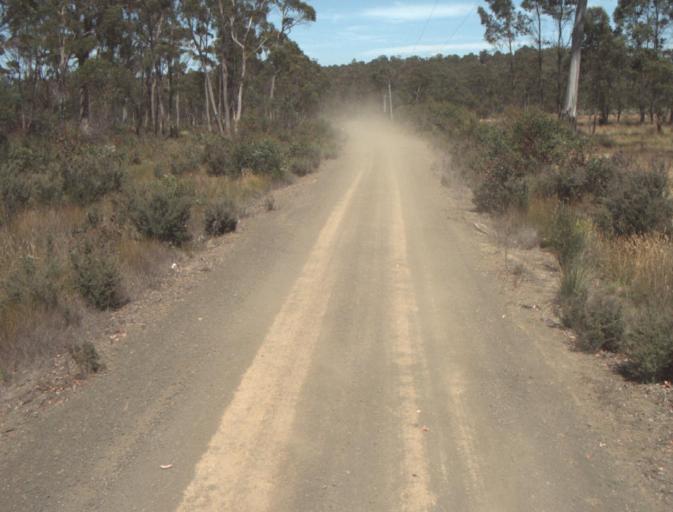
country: AU
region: Tasmania
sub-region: Launceston
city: Mayfield
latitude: -41.2744
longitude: 147.0991
